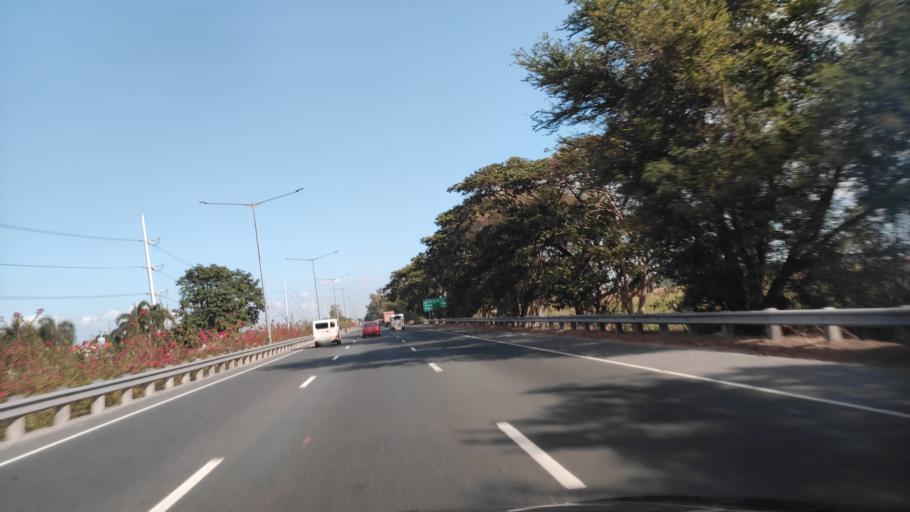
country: PH
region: Central Luzon
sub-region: Province of Pampanga
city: Pau
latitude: 15.0309
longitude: 120.7161
